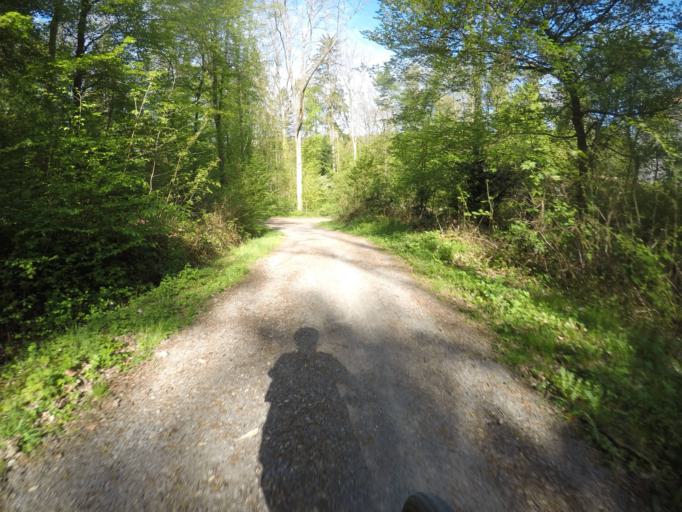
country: DE
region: Baden-Wuerttemberg
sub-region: Regierungsbezirk Stuttgart
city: Stuttgart
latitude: 48.7431
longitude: 9.1458
